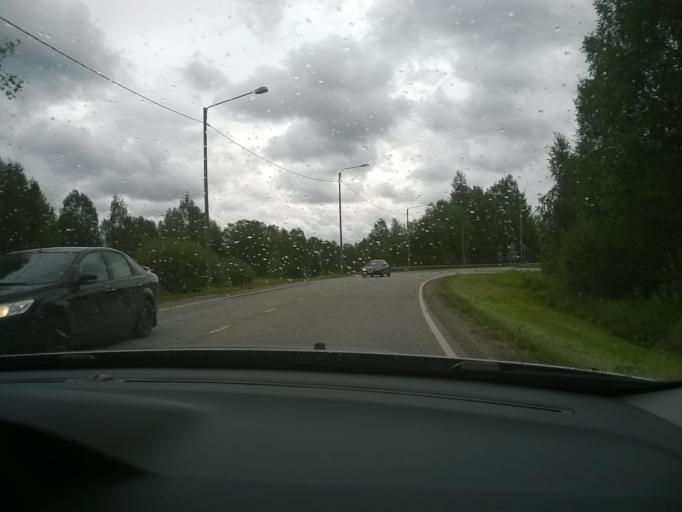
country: FI
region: Kainuu
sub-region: Kehys-Kainuu
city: Kuhmo
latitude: 64.1292
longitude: 29.5012
